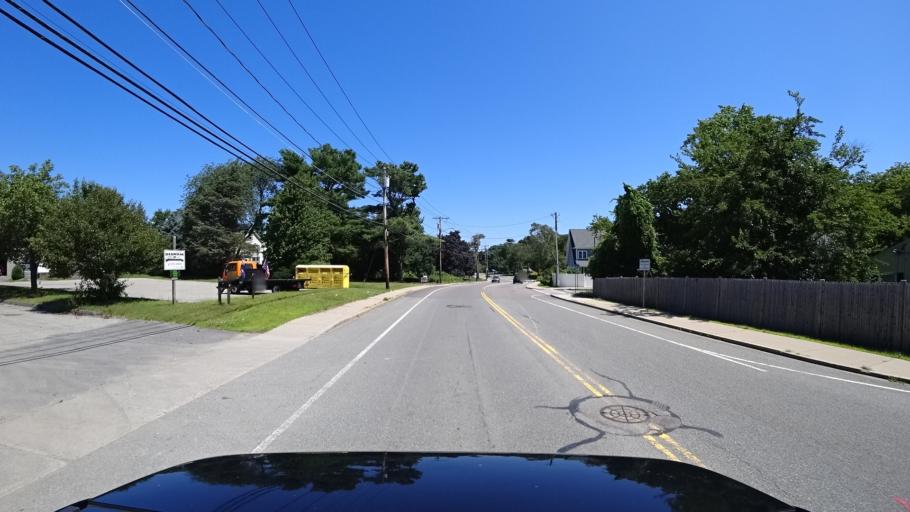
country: US
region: Massachusetts
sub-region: Norfolk County
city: Dedham
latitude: 42.2262
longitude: -71.1635
